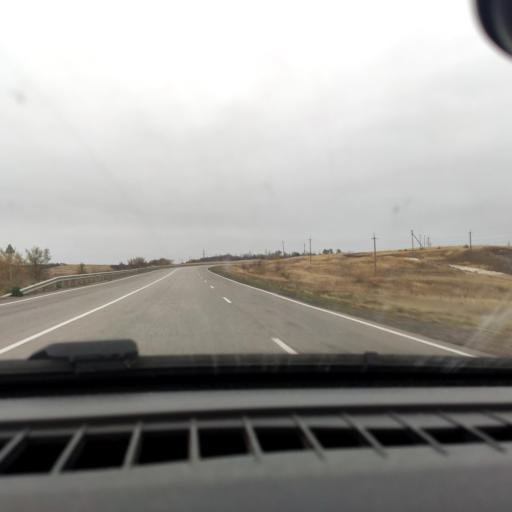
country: RU
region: Voronezj
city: Uryv-Pokrovka
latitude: 51.1335
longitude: 39.0461
